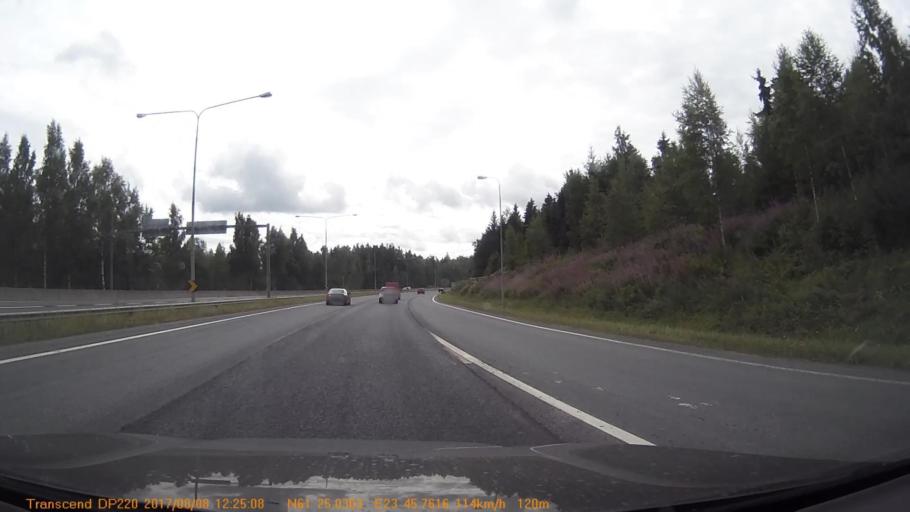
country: FI
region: Pirkanmaa
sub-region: Tampere
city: Tampere
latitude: 61.4169
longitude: 23.7631
